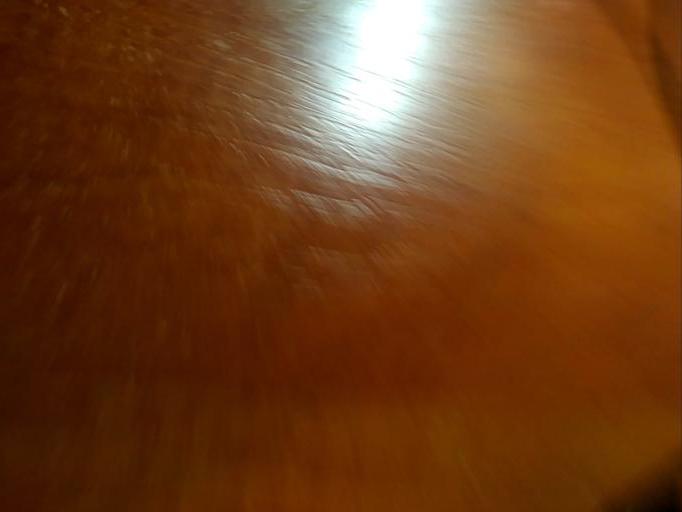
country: RU
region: Kaluga
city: Iznoski
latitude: 54.9547
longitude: 35.4304
